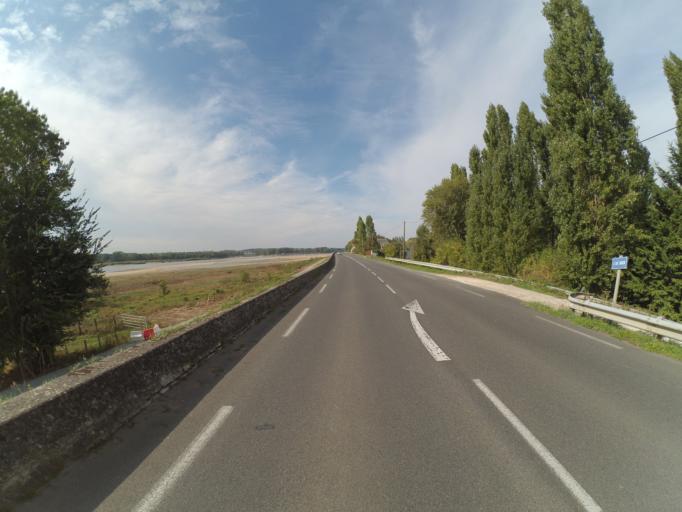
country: FR
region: Pays de la Loire
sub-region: Departement de Maine-et-Loire
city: Varennes-sur-Loire
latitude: 47.2381
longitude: 0.0210
